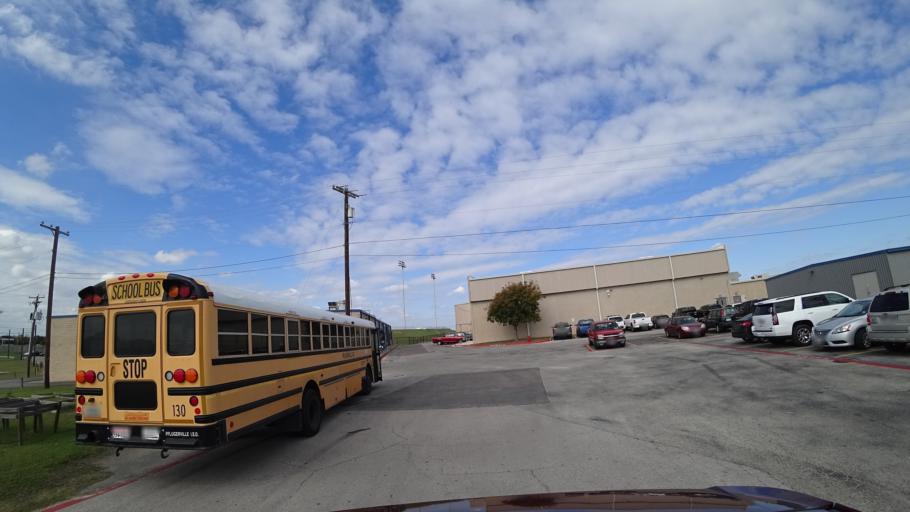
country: US
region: Texas
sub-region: Travis County
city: Pflugerville
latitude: 30.4436
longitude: -97.6337
